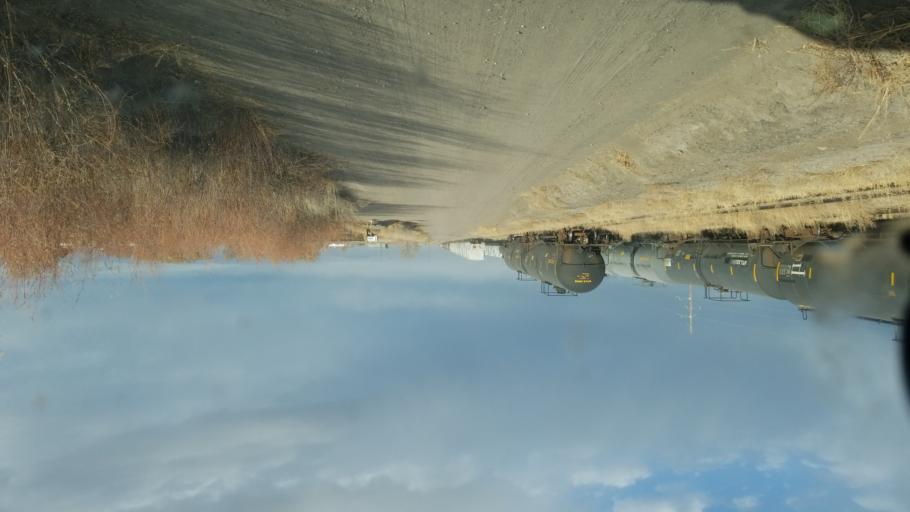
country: US
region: Colorado
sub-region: Alamosa County
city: Alamosa East
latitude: 37.4661
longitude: -105.8445
